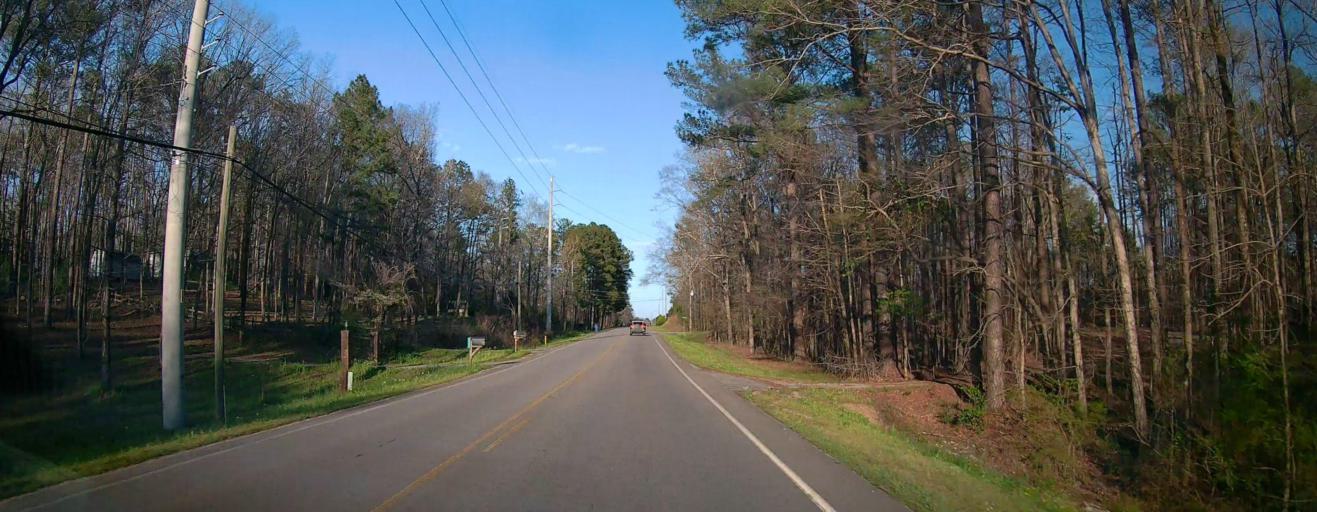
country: US
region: Alabama
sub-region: Shelby County
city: Indian Springs Village
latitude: 33.3260
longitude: -86.7038
